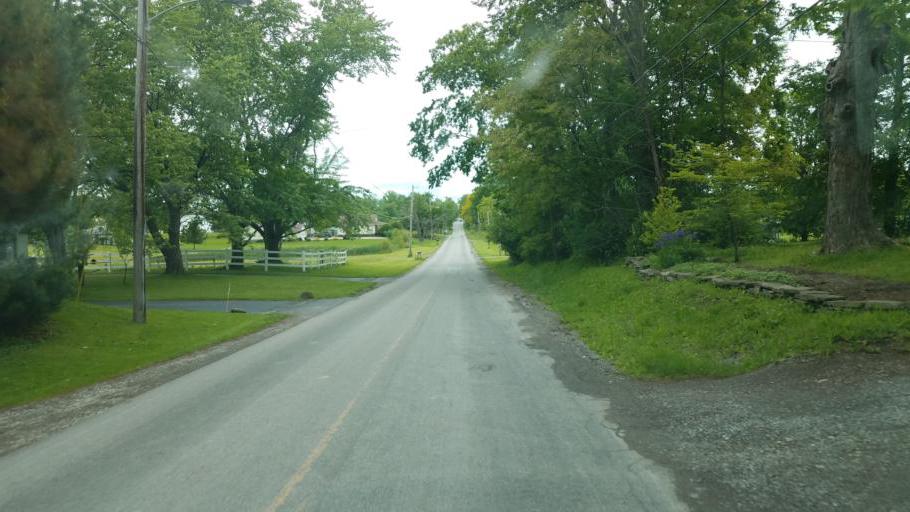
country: US
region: Ohio
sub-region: Geauga County
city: Middlefield
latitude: 41.3951
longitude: -80.9736
